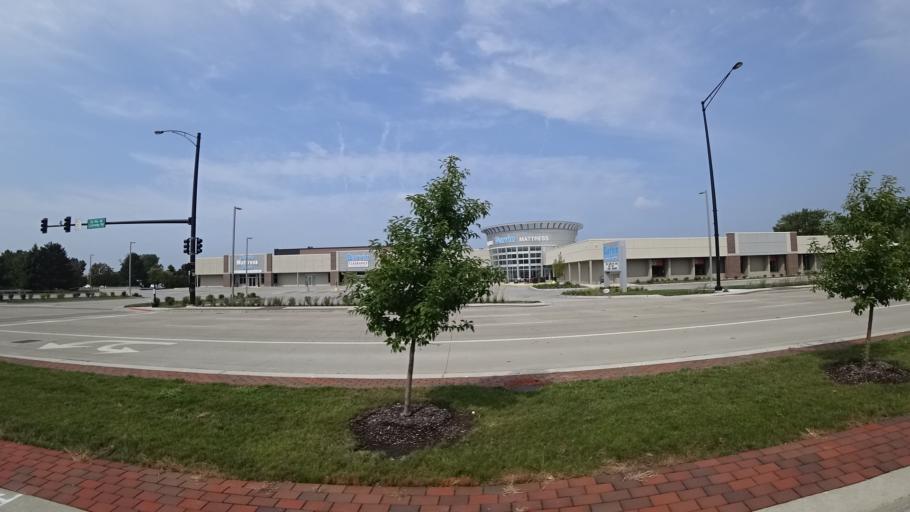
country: US
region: Illinois
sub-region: Cook County
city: Orland Park
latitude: 41.6105
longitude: -87.8531
